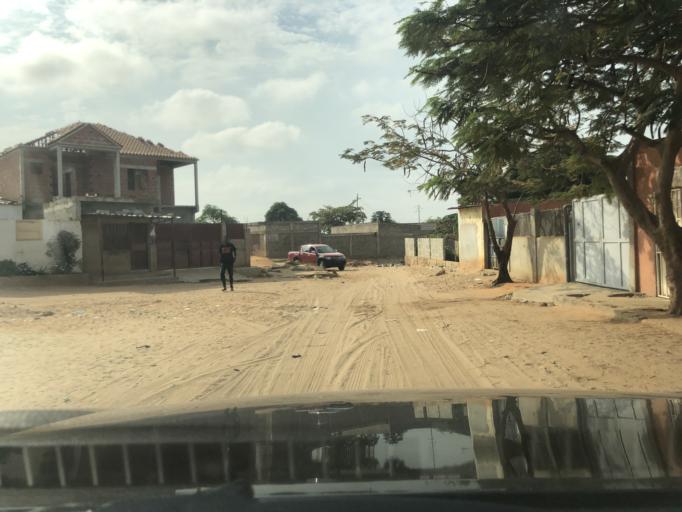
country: AO
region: Luanda
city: Luanda
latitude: -8.9375
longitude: 13.2379
